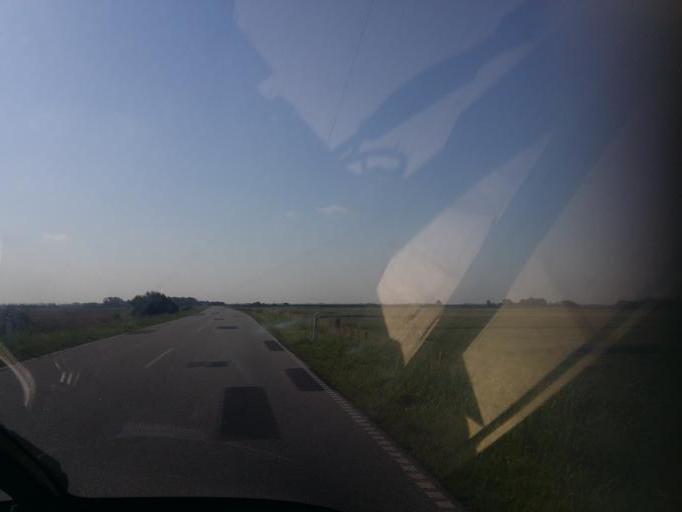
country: DE
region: Schleswig-Holstein
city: Rodenas
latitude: 54.9352
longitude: 8.7152
